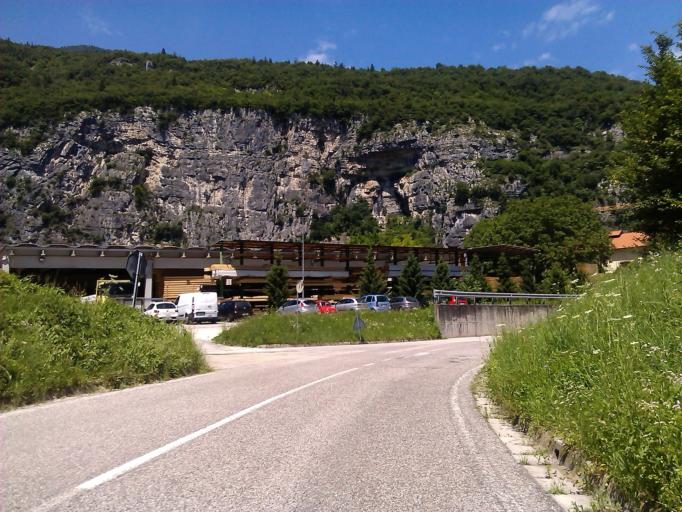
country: IT
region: Veneto
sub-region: Provincia di Vicenza
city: Enego
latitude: 45.9622
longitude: 11.7069
